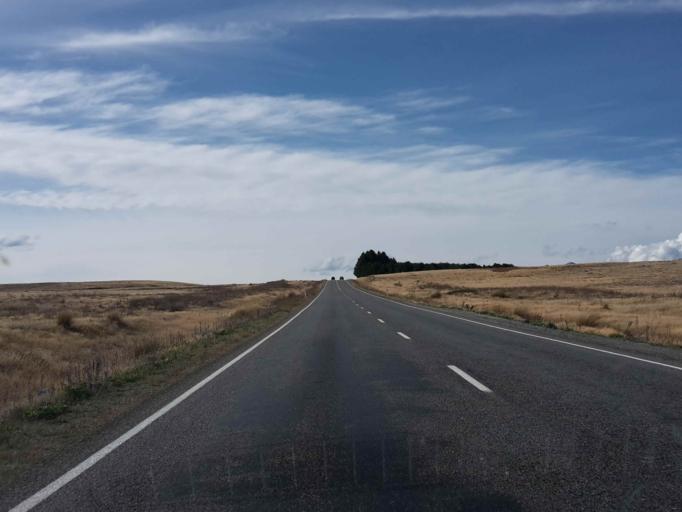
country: NZ
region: Canterbury
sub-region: Timaru District
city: Pleasant Point
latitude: -44.0371
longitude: 170.3846
